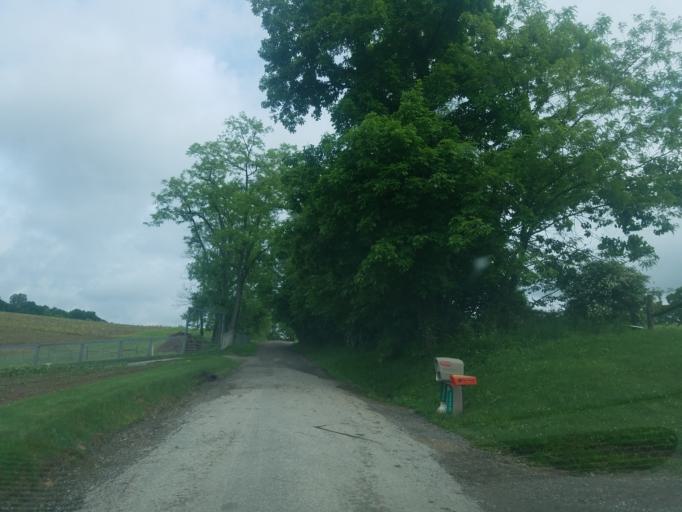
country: US
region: Ohio
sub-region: Holmes County
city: Millersburg
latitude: 40.4809
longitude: -81.8127
